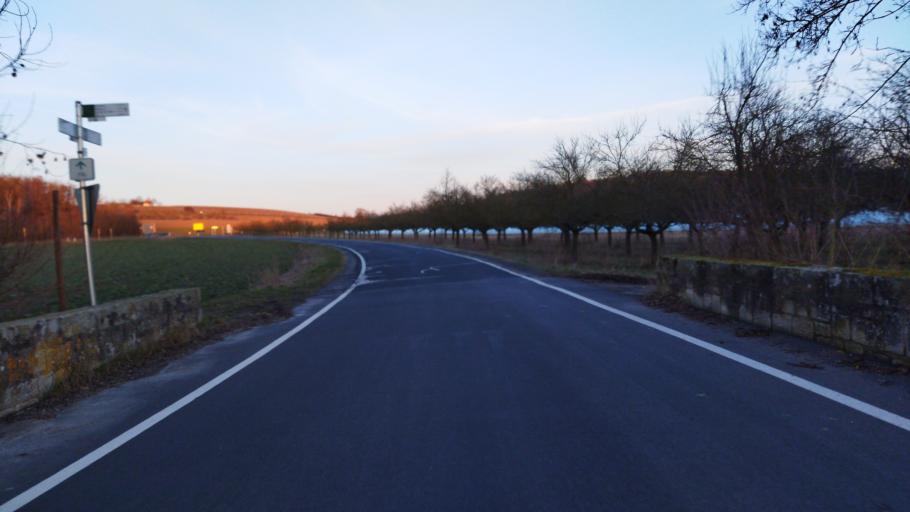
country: DE
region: Bavaria
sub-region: Regierungsbezirk Unterfranken
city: Wipfeld
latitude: 49.9203
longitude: 10.1850
